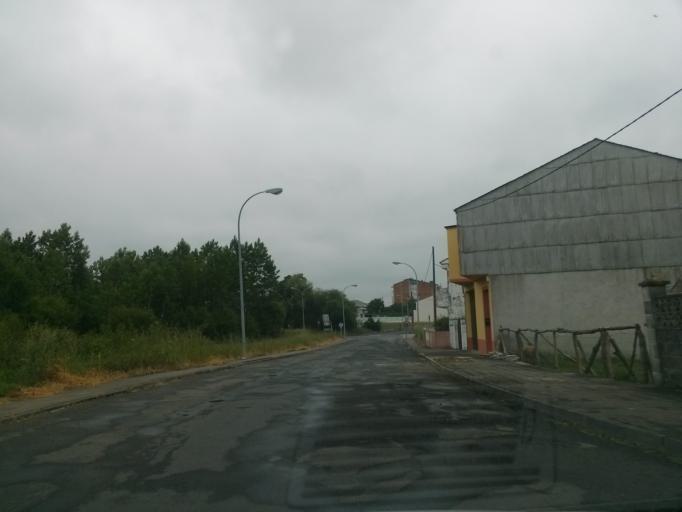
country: ES
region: Galicia
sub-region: Provincia de Lugo
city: Rabade
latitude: 43.1227
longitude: -7.6295
